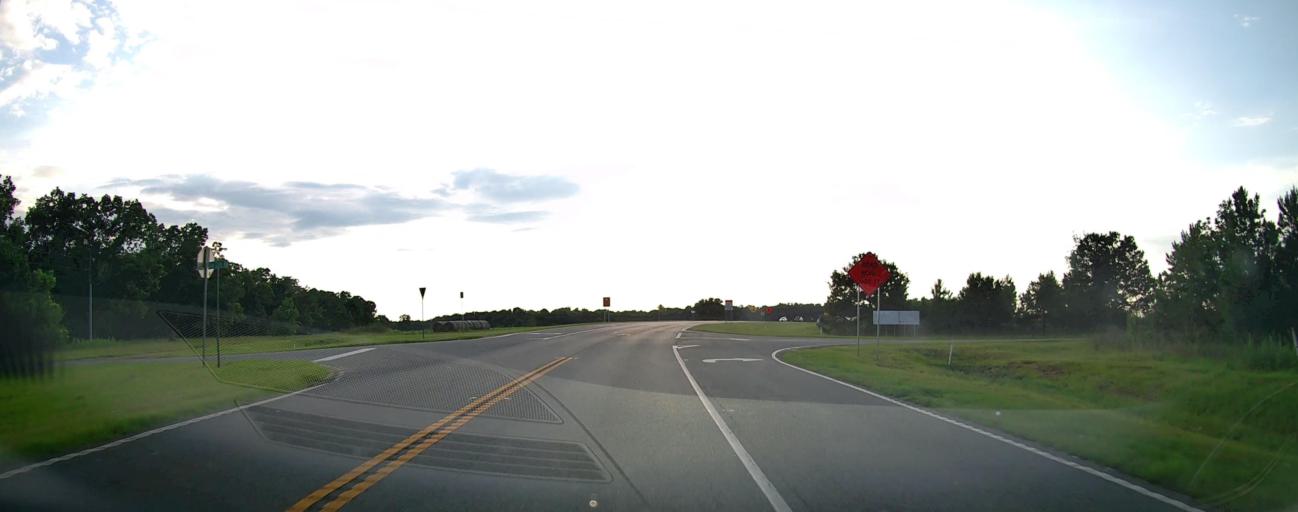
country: US
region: Georgia
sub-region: Peach County
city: Fort Valley
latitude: 32.5585
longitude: -83.9359
